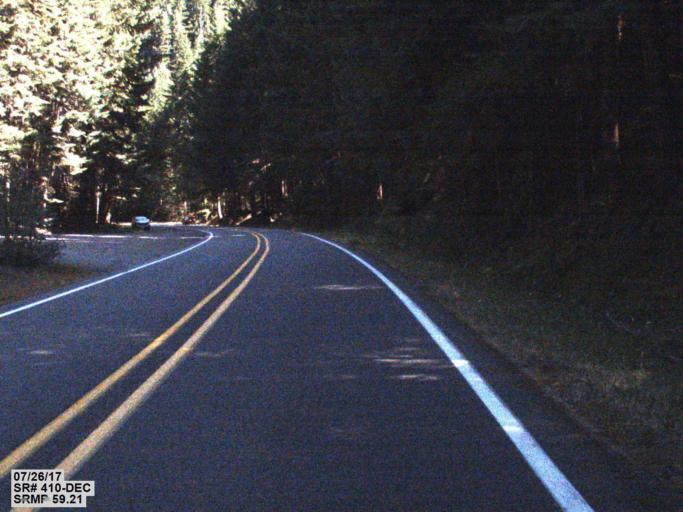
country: US
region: Washington
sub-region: King County
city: Enumclaw
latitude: 46.9566
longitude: -121.5261
